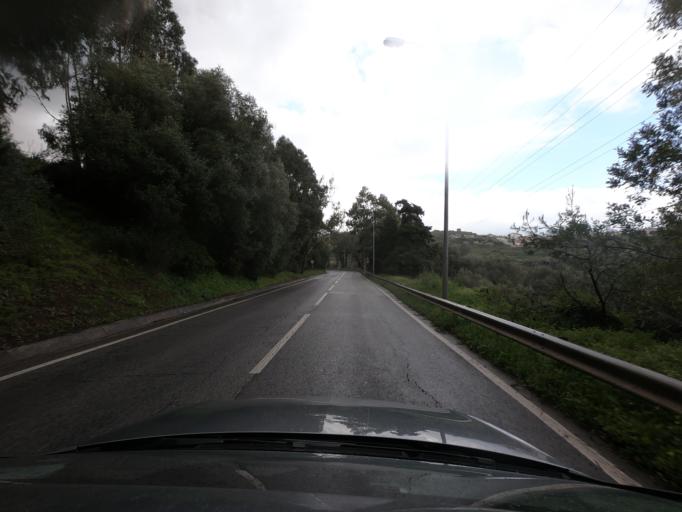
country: PT
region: Lisbon
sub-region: Oeiras
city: Carnaxide
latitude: 38.7275
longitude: -9.2565
